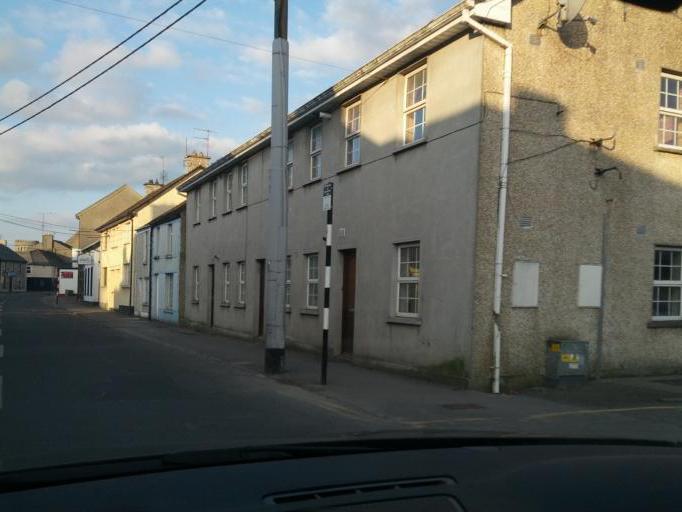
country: IE
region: Munster
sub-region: North Tipperary
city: Nenagh
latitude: 52.8611
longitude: -8.2025
